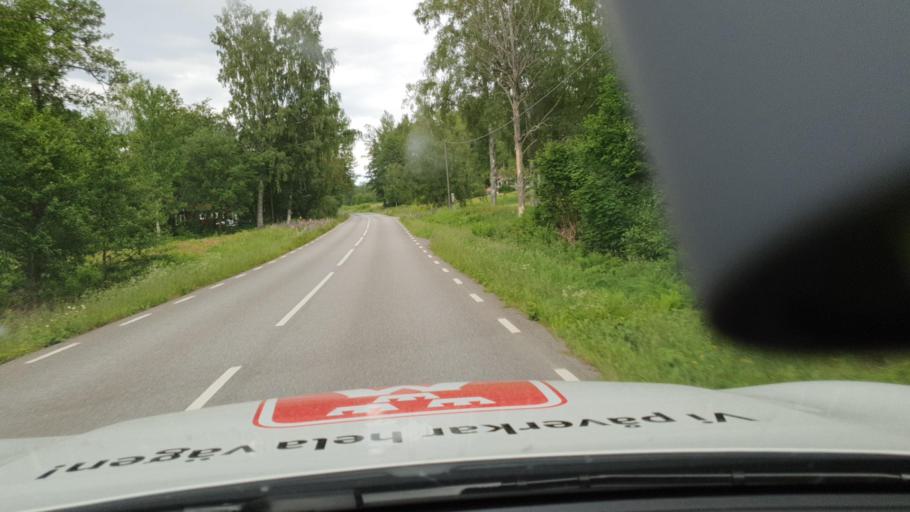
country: SE
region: Vaestra Goetaland
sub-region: Karlsborgs Kommun
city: Karlsborg
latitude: 58.7625
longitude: 14.5213
